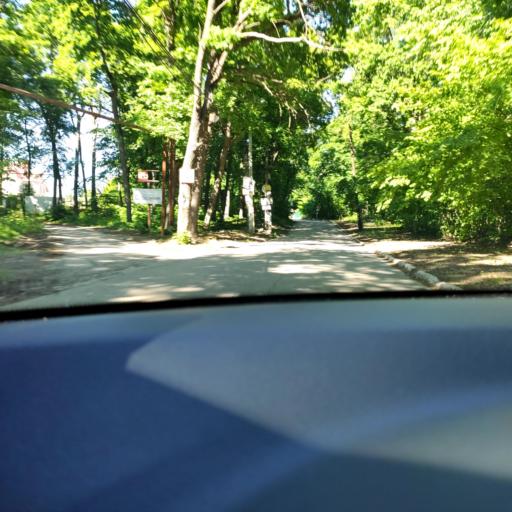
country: RU
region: Samara
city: Samara
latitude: 53.2899
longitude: 50.1977
